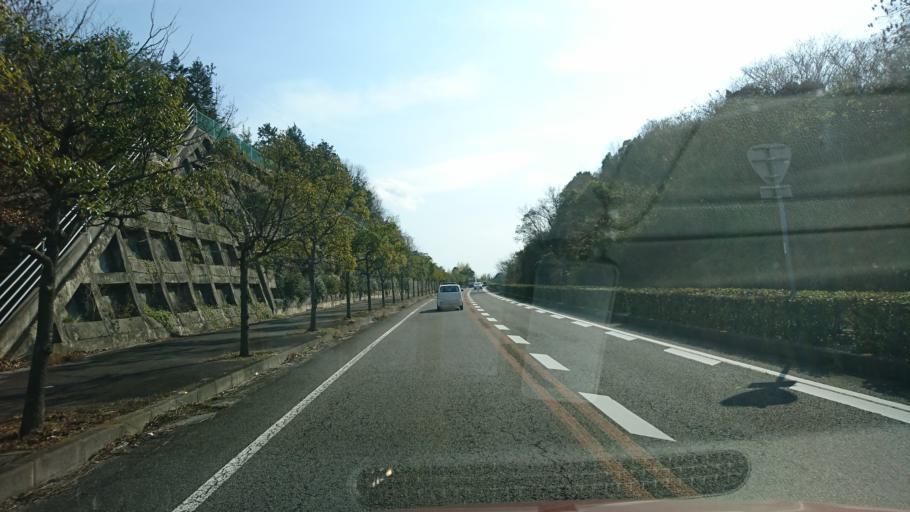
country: JP
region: Ehime
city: Saijo
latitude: 34.0157
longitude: 133.0324
